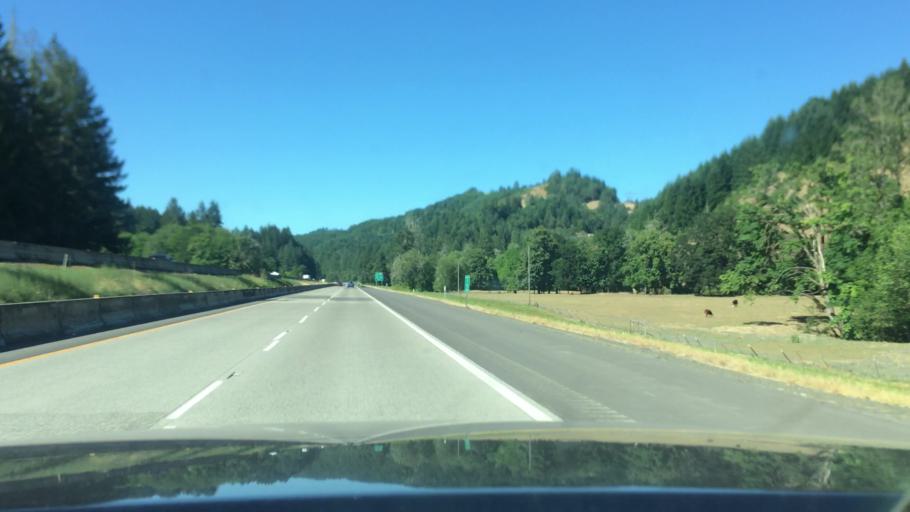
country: US
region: Oregon
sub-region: Douglas County
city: Yoncalla
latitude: 43.6531
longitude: -123.2086
